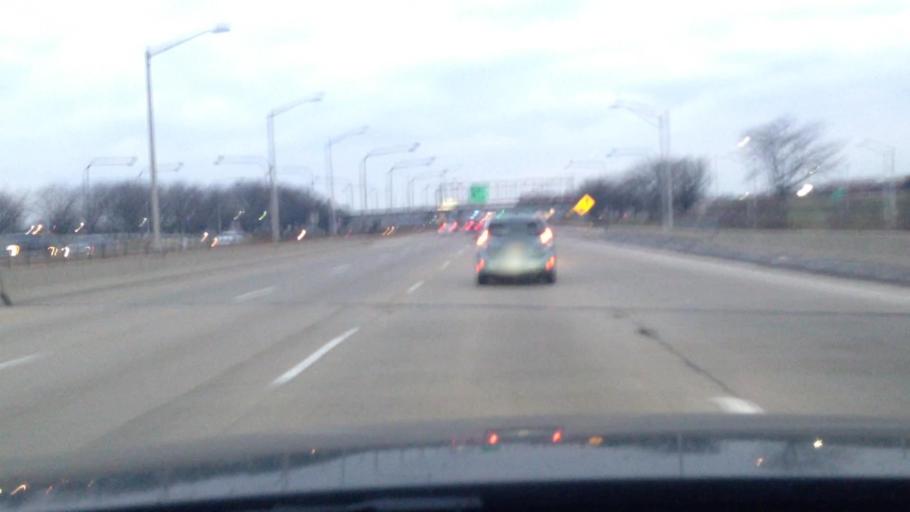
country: US
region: Illinois
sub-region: Cook County
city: Rosemont
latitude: 41.9778
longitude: -87.8861
